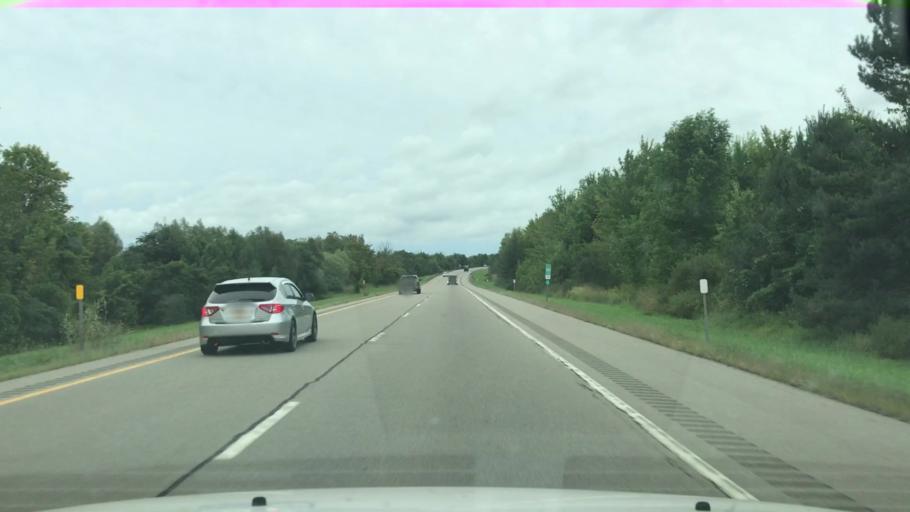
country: US
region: New York
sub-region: Erie County
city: North Boston
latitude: 42.6444
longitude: -78.7647
